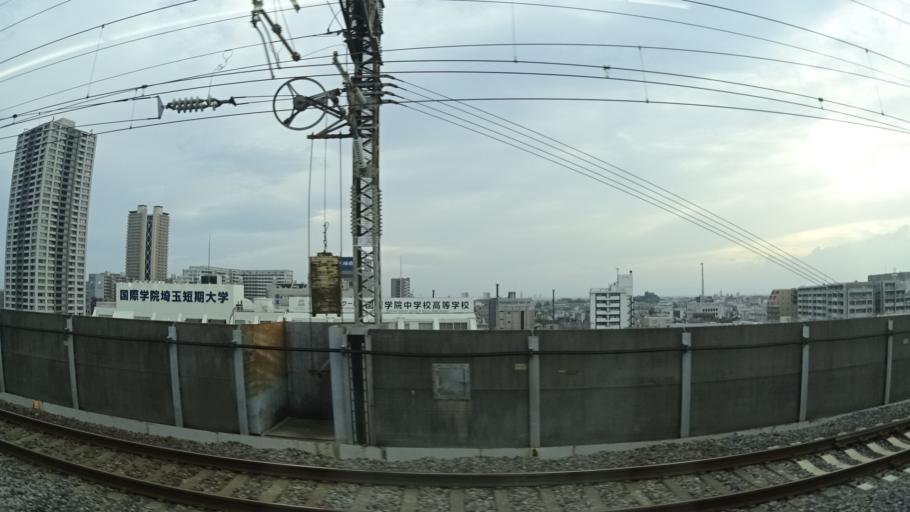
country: JP
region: Saitama
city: Yono
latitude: 35.9009
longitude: 139.6266
